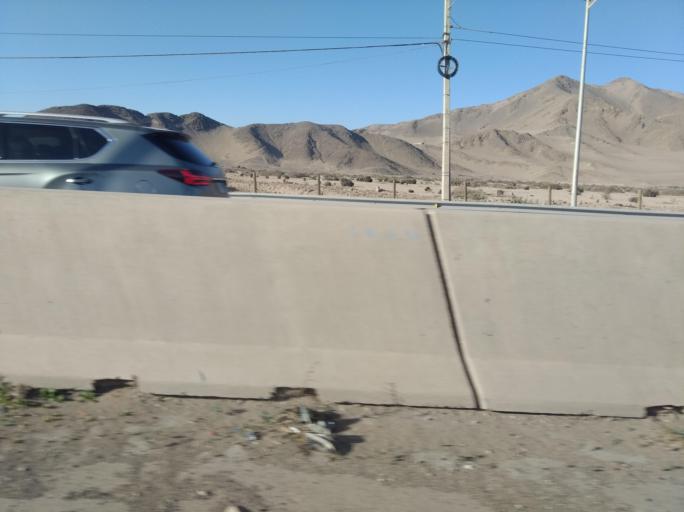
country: CL
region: Atacama
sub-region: Provincia de Copiapo
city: Copiapo
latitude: -27.3401
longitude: -70.3733
